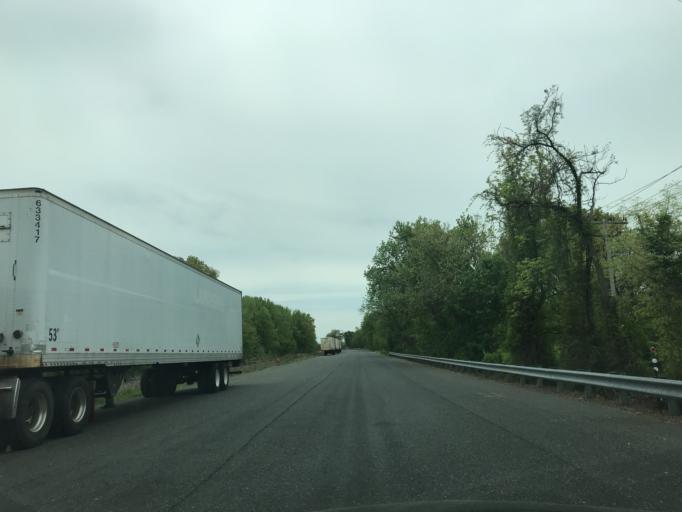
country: US
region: Maryland
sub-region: Baltimore County
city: Edgemere
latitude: 39.2498
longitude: -76.4682
